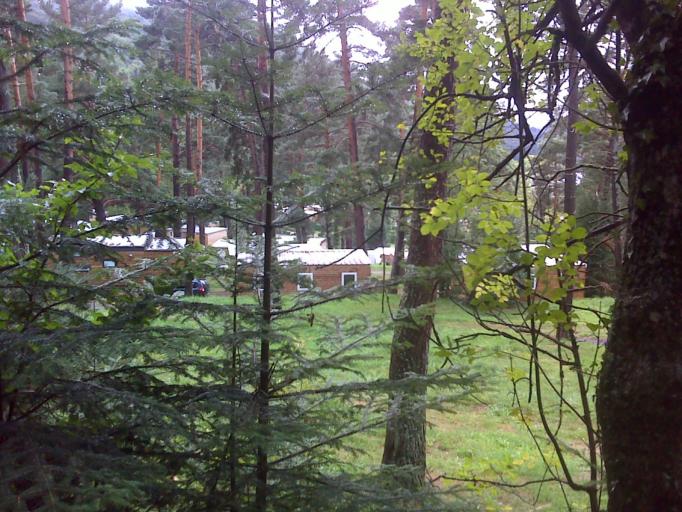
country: FR
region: Auvergne
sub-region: Departement du Puy-de-Dome
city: Aydat
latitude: 45.5692
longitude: 2.9332
